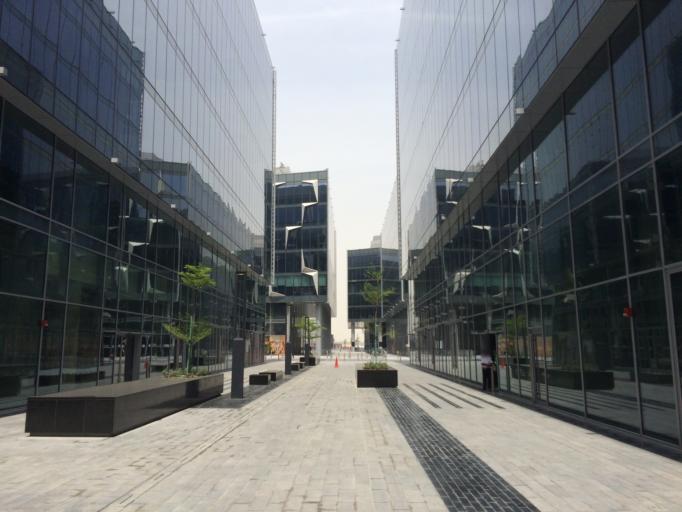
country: AE
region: Dubai
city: Dubai
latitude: 25.1872
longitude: 55.2972
